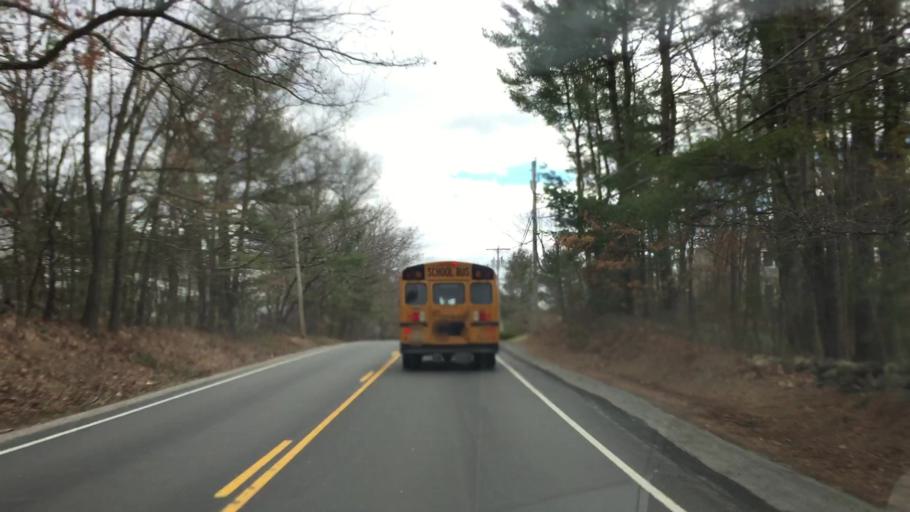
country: US
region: New Hampshire
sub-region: Rockingham County
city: Londonderry
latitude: 42.8234
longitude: -71.3642
